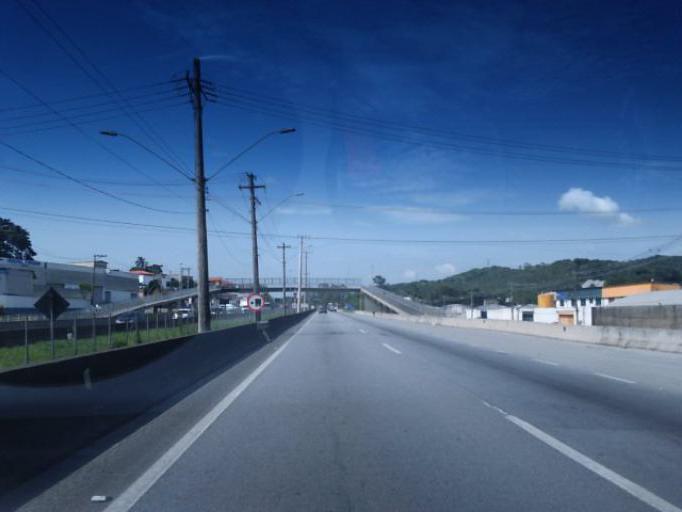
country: BR
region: Sao Paulo
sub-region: Itapecerica Da Serra
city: Itapecerica da Serra
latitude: -23.6867
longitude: -46.8605
